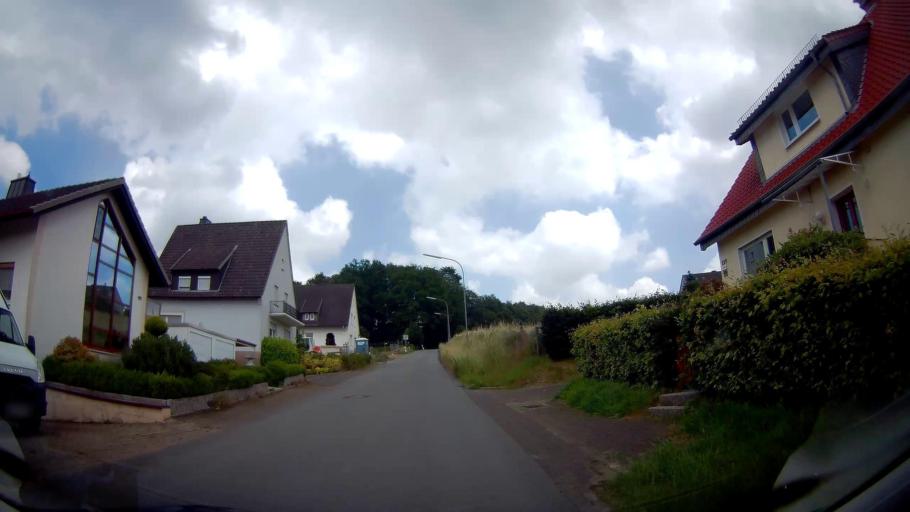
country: DE
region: North Rhine-Westphalia
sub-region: Regierungsbezirk Detmold
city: Herford
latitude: 52.1289
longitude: 8.7145
